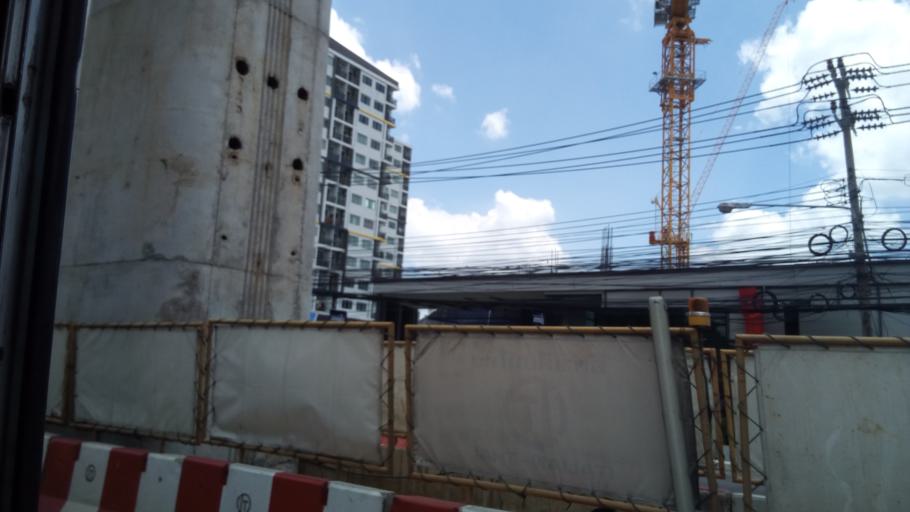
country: TH
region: Bangkok
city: Lak Si
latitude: 13.8792
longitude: 100.5990
